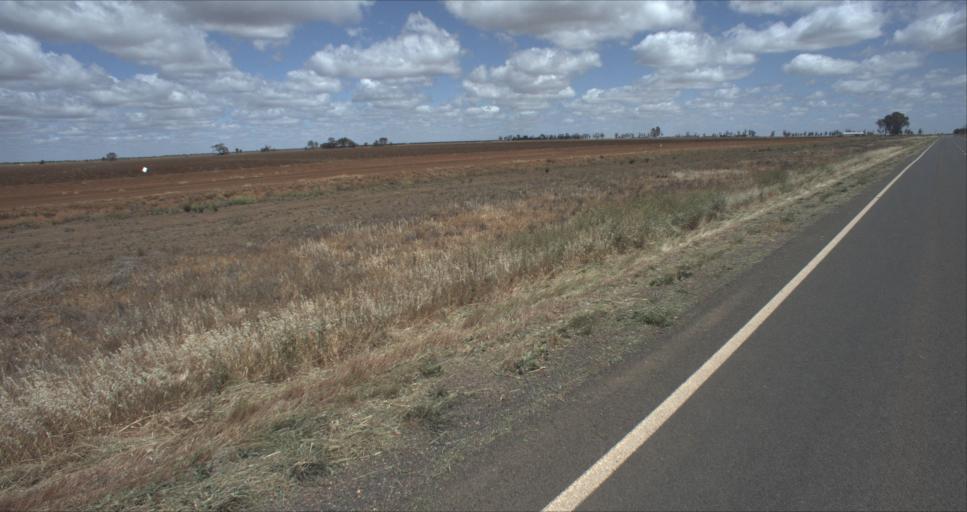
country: AU
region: New South Wales
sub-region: Murrumbidgee Shire
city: Darlington Point
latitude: -34.4727
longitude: 146.1436
